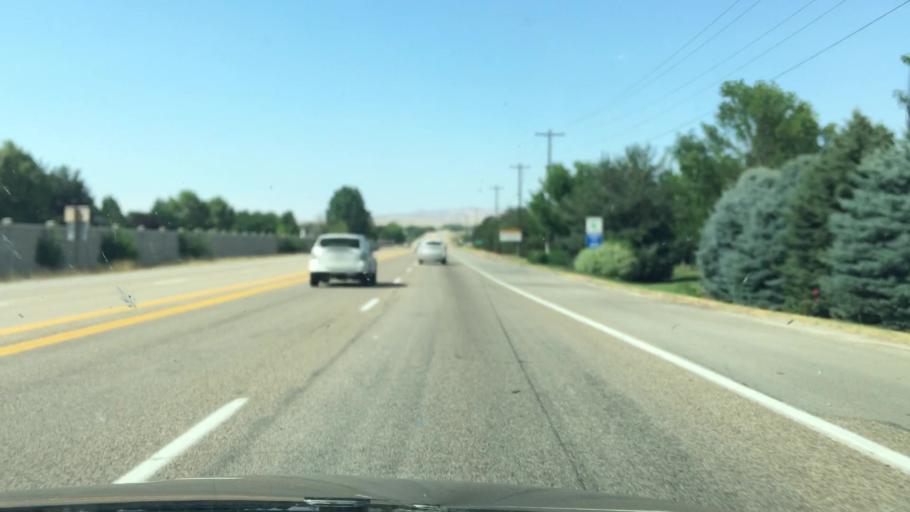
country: US
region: Idaho
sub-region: Ada County
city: Eagle
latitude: 43.6868
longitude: -116.3192
